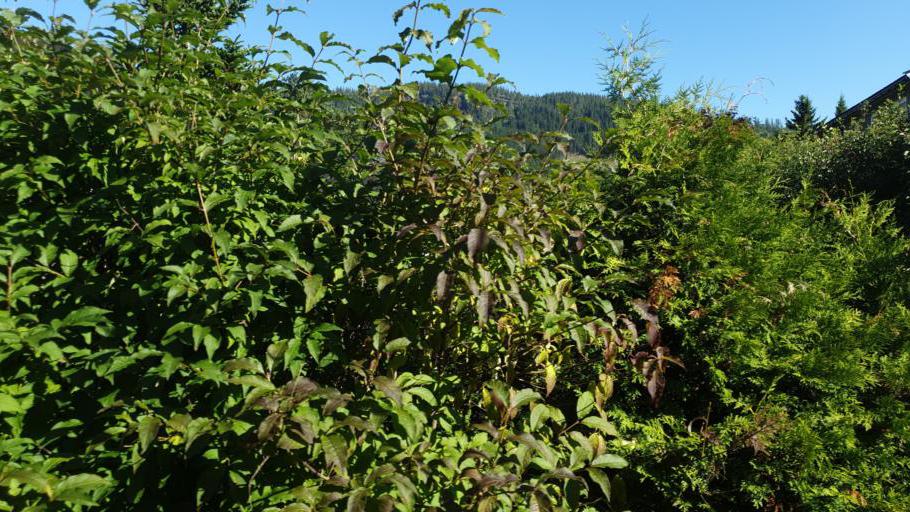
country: NO
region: Sor-Trondelag
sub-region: Orkdal
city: Orkanger
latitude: 63.2763
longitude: 9.8242
